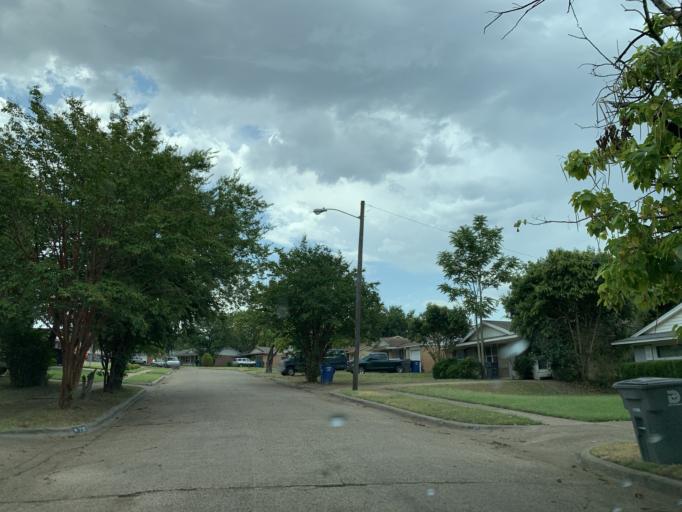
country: US
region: Texas
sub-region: Dallas County
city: Duncanville
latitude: 32.6645
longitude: -96.8337
